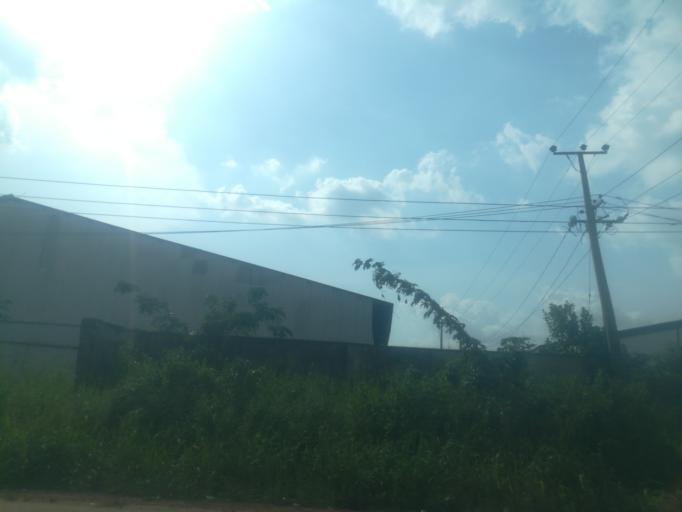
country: NG
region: Ogun
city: Abeokuta
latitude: 7.1138
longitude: 3.2974
